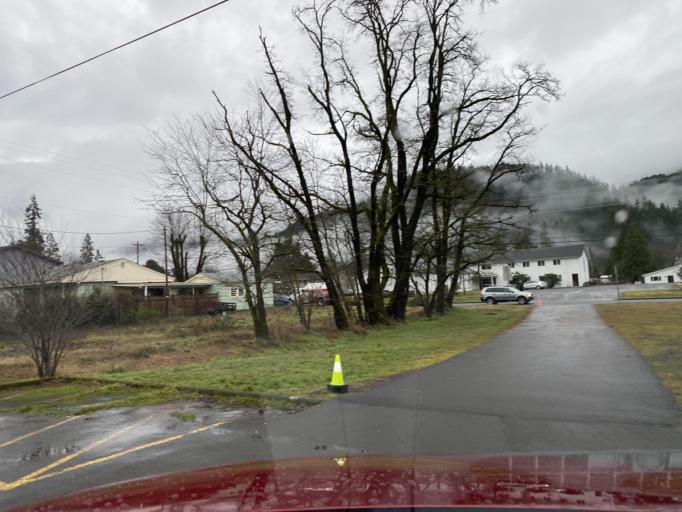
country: US
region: Oregon
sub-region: Lane County
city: Oakridge
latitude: 43.7461
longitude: -122.4849
